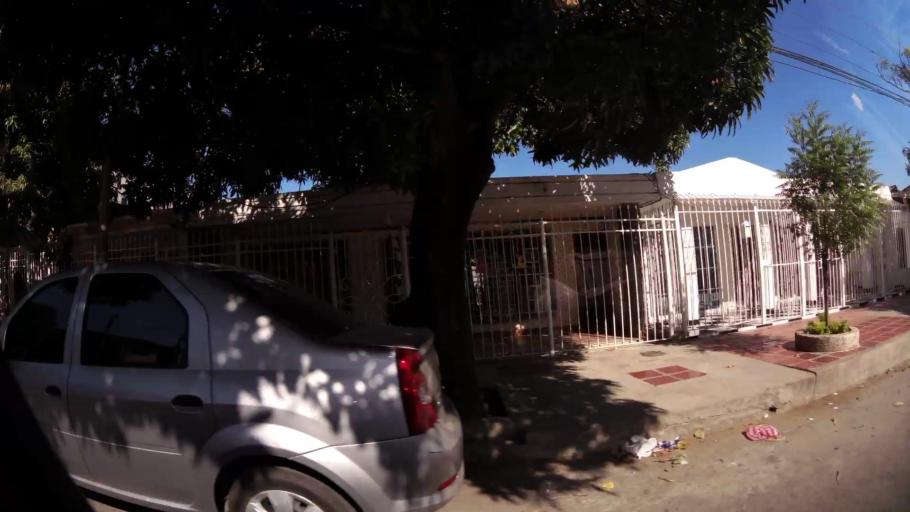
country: CO
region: Atlantico
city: Barranquilla
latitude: 10.9478
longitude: -74.7925
